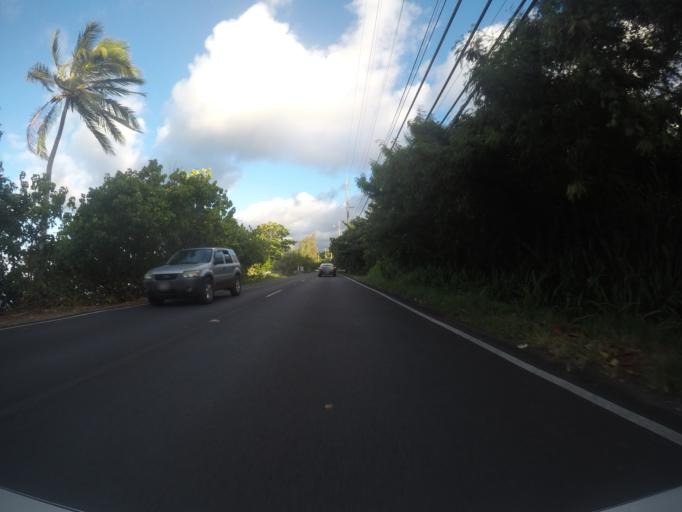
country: US
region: Hawaii
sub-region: Honolulu County
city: He'eia
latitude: 21.4456
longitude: -157.8134
